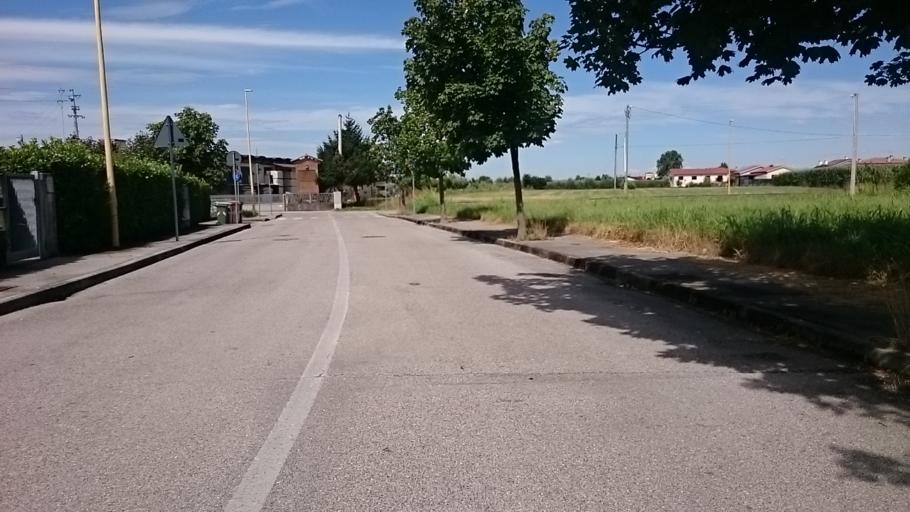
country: IT
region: Veneto
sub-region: Provincia di Padova
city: Ponte San Nicolo
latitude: 45.3646
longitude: 11.9060
